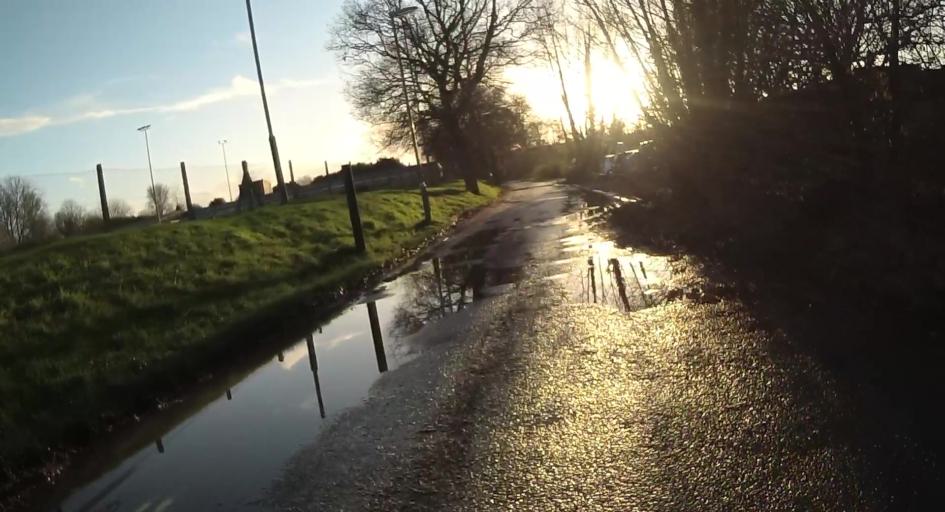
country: GB
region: England
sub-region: Hampshire
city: Winchester
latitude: 51.0720
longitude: -1.3086
